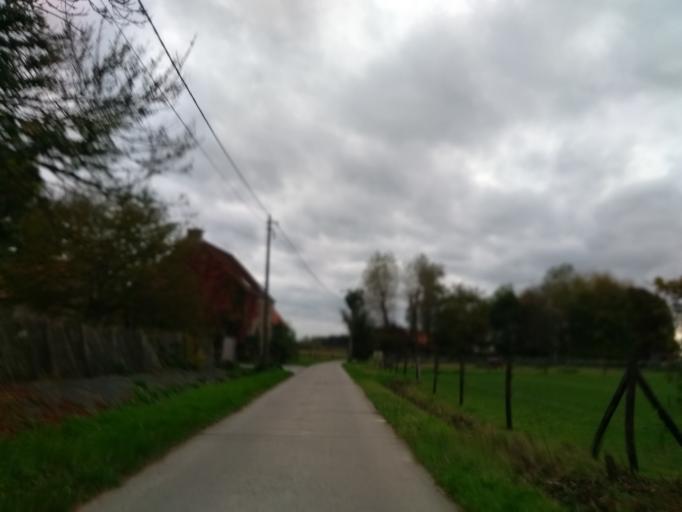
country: BE
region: Flanders
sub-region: Provincie Oost-Vlaanderen
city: Oosterzele
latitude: 50.9279
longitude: 3.7708
